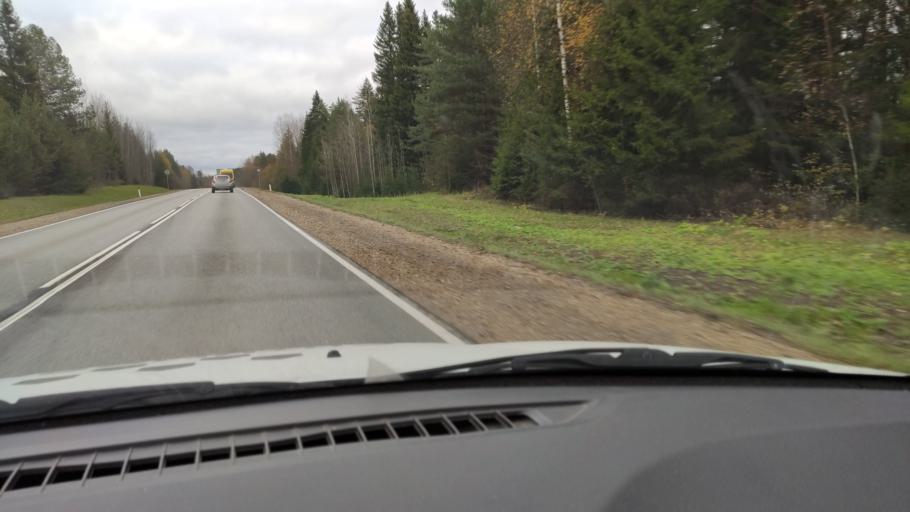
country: RU
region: Kirov
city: Slobodskoy
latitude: 58.7713
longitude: 50.3732
